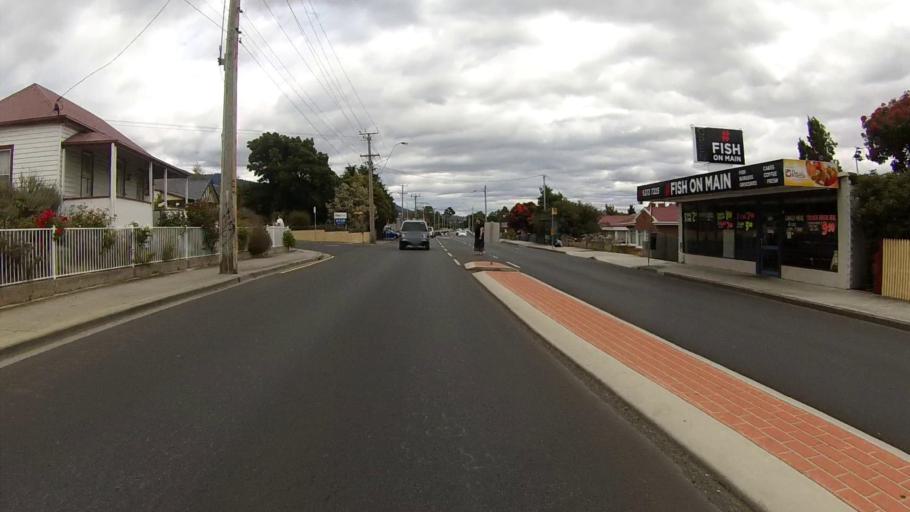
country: AU
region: Tasmania
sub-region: Glenorchy
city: Glenorchy
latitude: -42.8268
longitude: 147.2669
